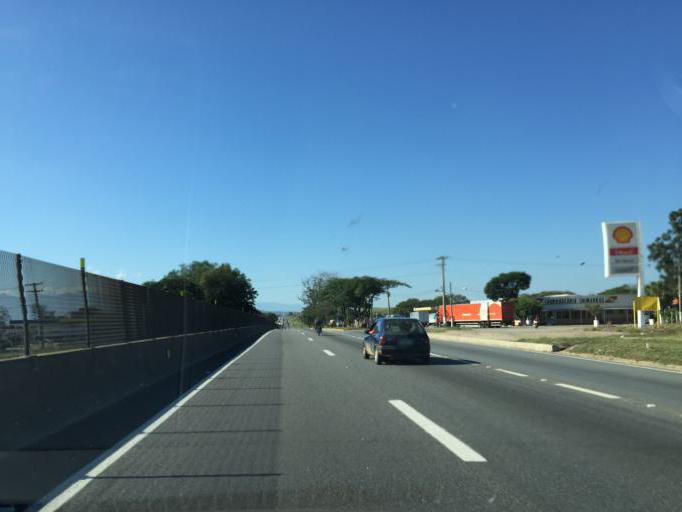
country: BR
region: Sao Paulo
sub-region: Lorena
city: Lorena
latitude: -22.7134
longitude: -45.0526
